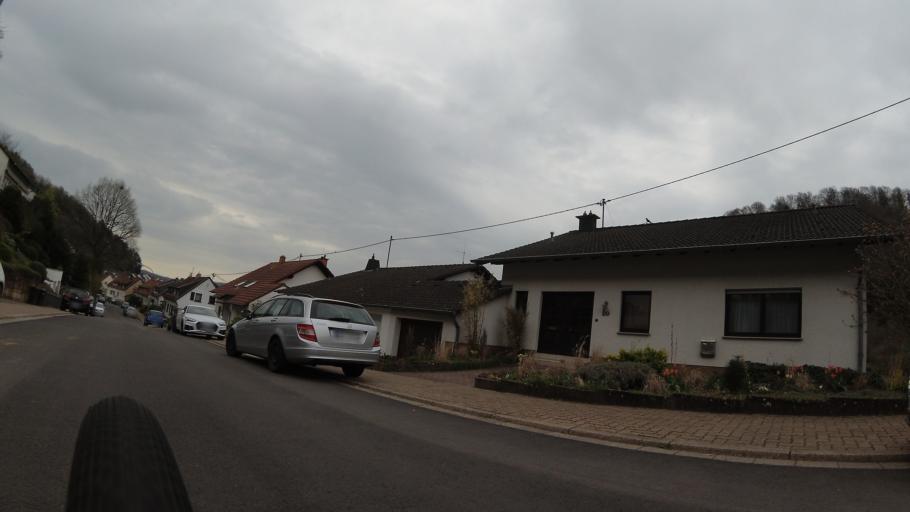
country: DE
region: Saarland
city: Merzig
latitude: 49.4584
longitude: 6.6432
